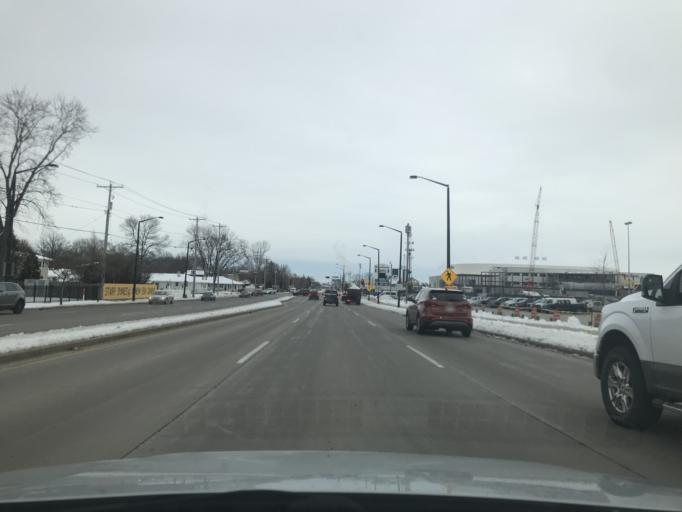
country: US
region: Wisconsin
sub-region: Brown County
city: Ashwaubenon
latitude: 44.5022
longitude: -88.0588
